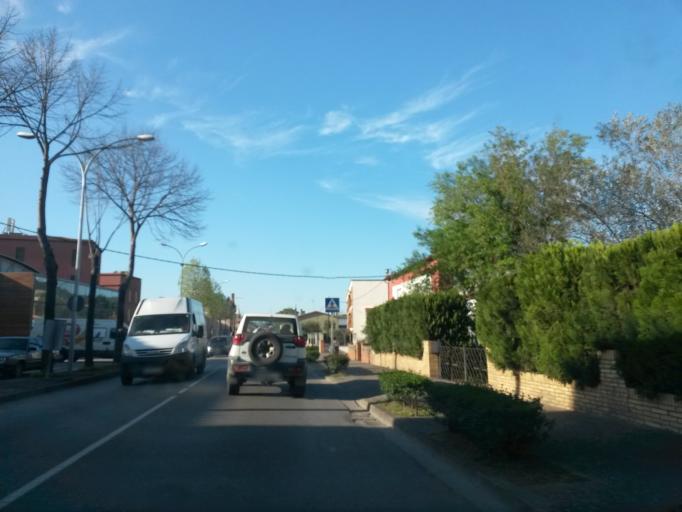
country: ES
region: Catalonia
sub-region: Provincia de Girona
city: Sarria de Ter
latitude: 42.0081
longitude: 2.8250
